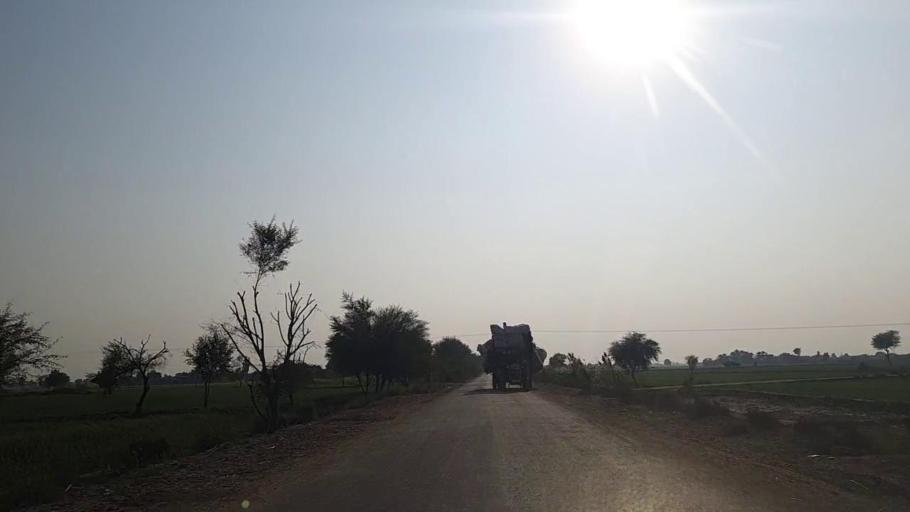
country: PK
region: Sindh
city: Jam Sahib
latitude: 26.2804
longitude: 68.6189
